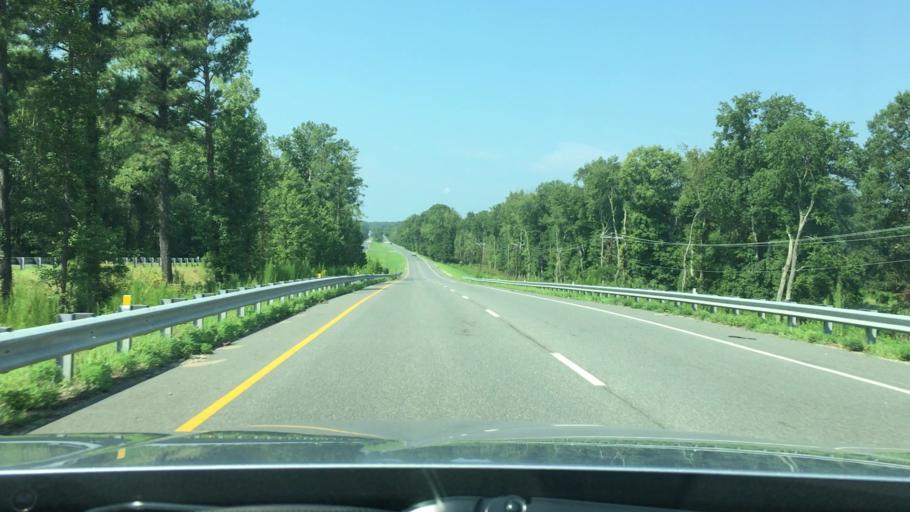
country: US
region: Virginia
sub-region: Caroline County
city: Bowling Green
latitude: 38.0323
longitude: -77.3770
